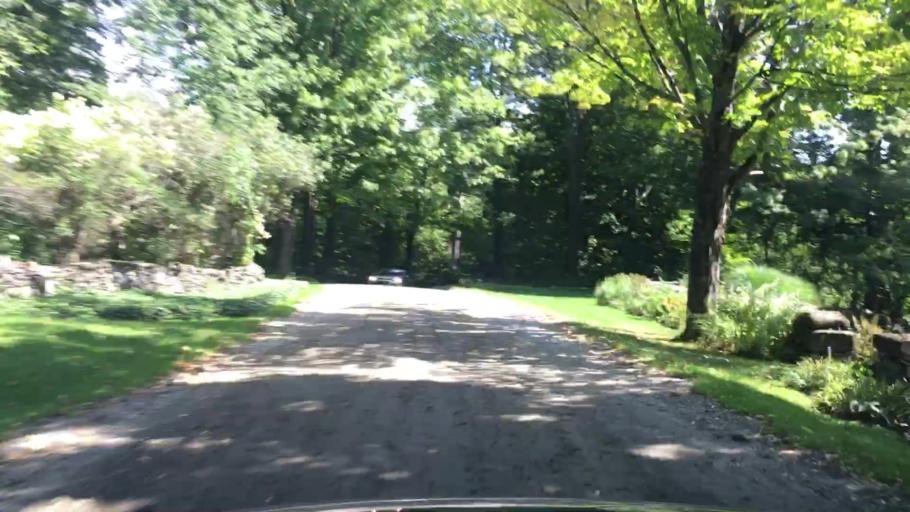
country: US
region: Vermont
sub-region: Windham County
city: West Brattleboro
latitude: 42.8025
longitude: -72.6491
